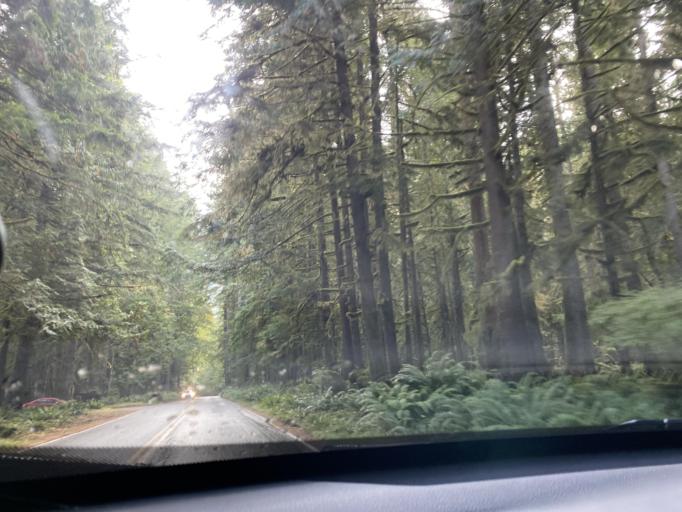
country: CA
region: British Columbia
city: Sooke
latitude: 48.0576
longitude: -123.7932
